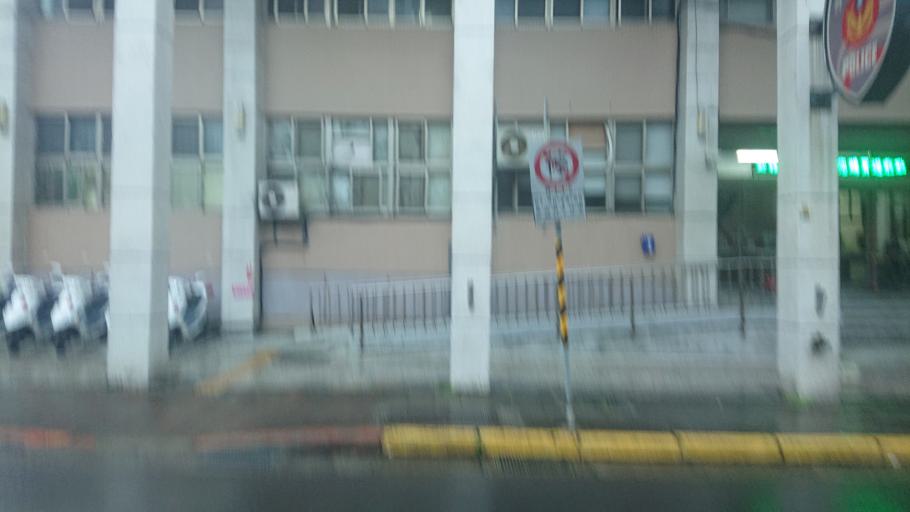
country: TW
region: Taipei
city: Taipei
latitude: 24.9888
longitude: 121.5638
